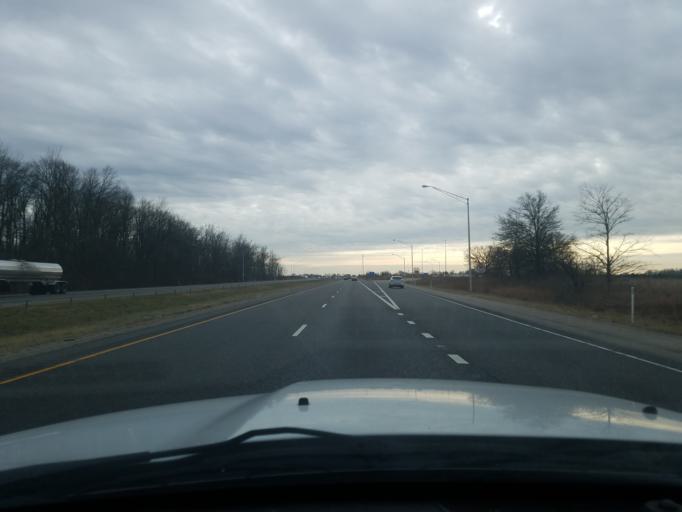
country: US
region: Indiana
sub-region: Grant County
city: Fairmount
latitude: 40.3633
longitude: -85.5590
